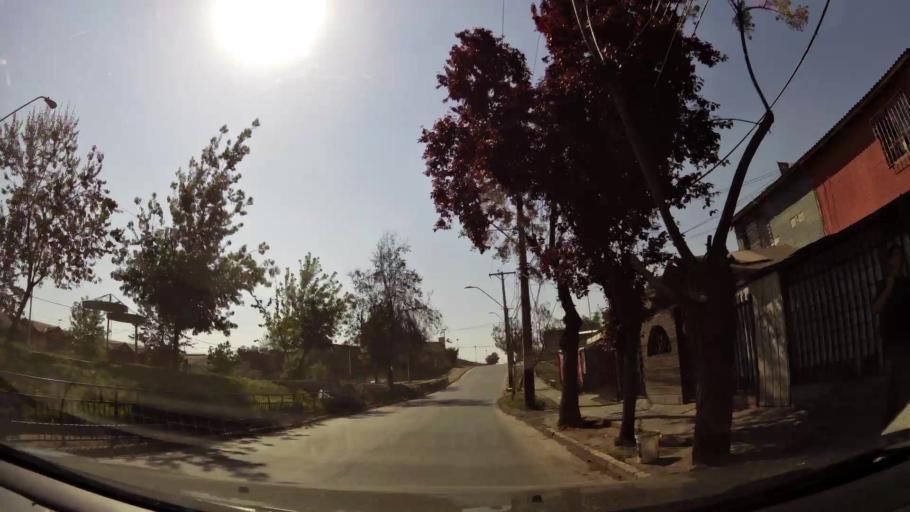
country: CL
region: Santiago Metropolitan
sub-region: Provincia de Cordillera
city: Puente Alto
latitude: -33.6294
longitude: -70.6193
